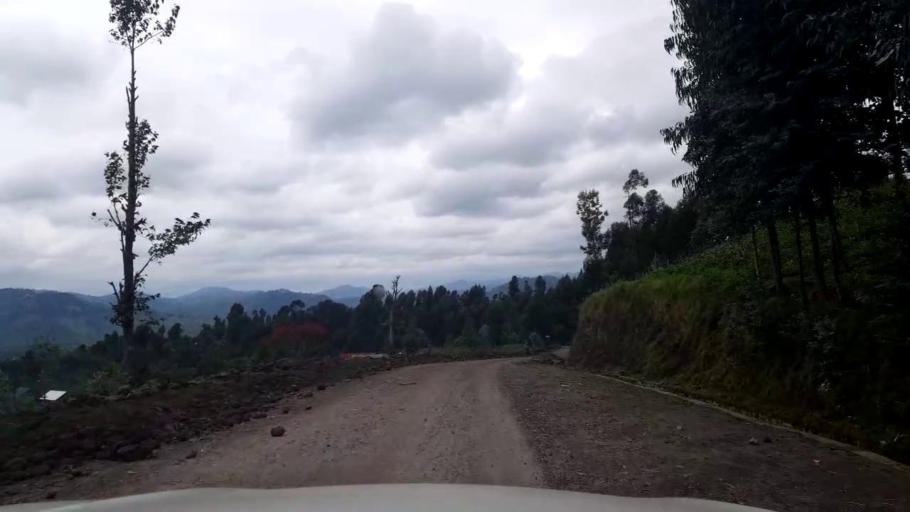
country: RW
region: Northern Province
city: Musanze
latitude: -1.5369
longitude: 29.5333
